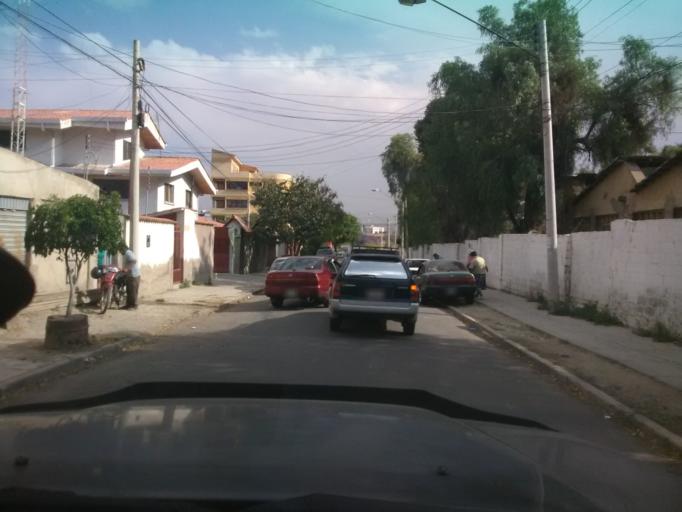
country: BO
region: Cochabamba
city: Cochabamba
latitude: -17.3769
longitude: -66.1478
